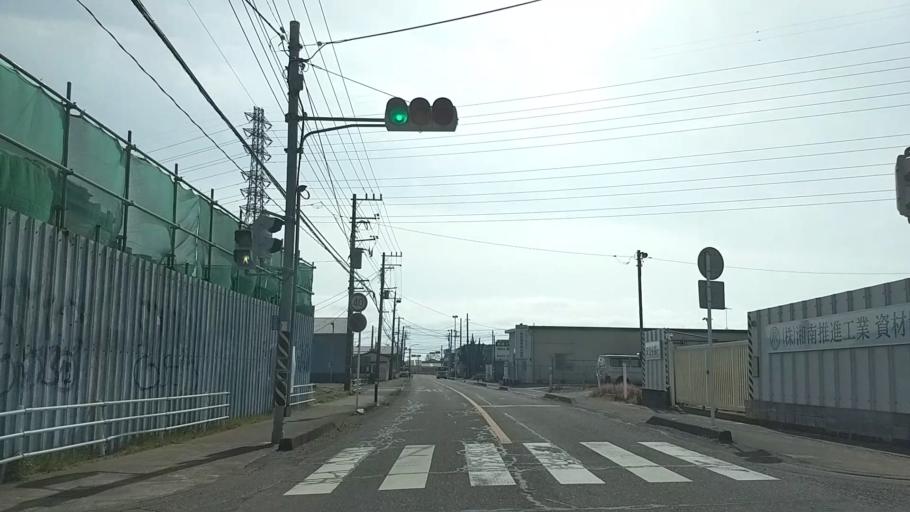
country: JP
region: Kanagawa
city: Chigasaki
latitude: 35.3592
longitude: 139.3846
